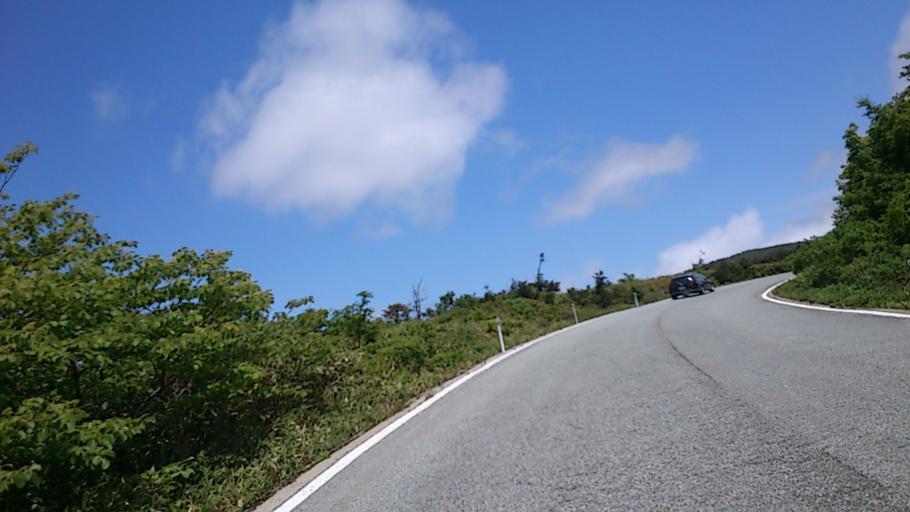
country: JP
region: Yamagata
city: Yamagata-shi
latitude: 38.1242
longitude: 140.4218
